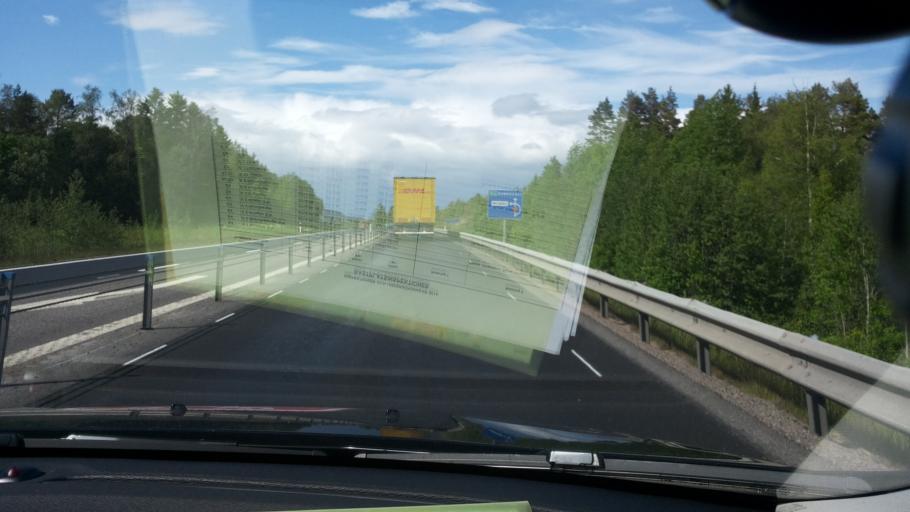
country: SE
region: Vaesternorrland
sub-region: Sundsvalls Kommun
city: Njurundabommen
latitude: 62.2348
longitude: 17.3749
